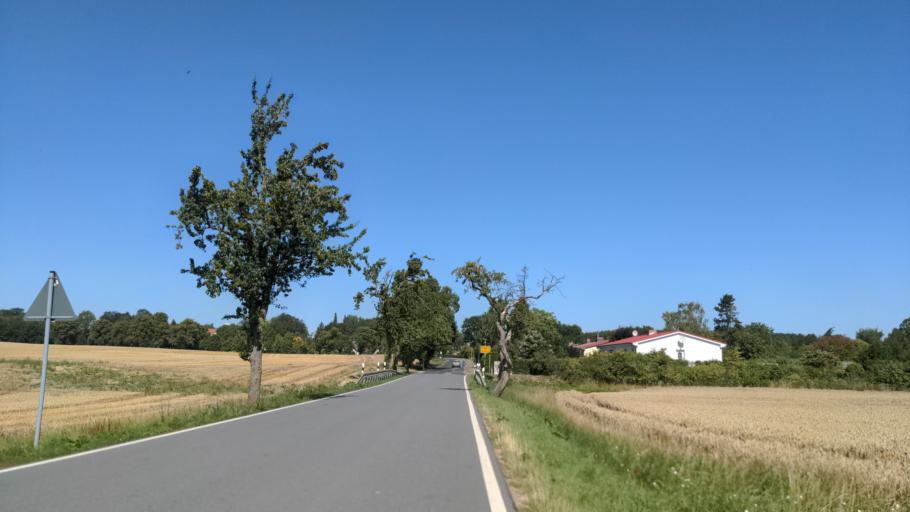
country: DE
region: Mecklenburg-Vorpommern
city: Klutz
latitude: 53.9903
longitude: 11.1256
